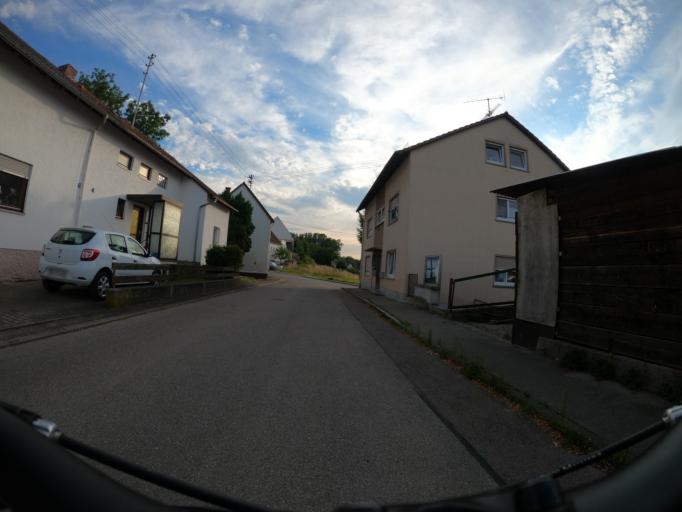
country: DE
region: Bavaria
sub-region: Swabia
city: Nersingen
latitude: 48.4319
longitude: 10.1612
